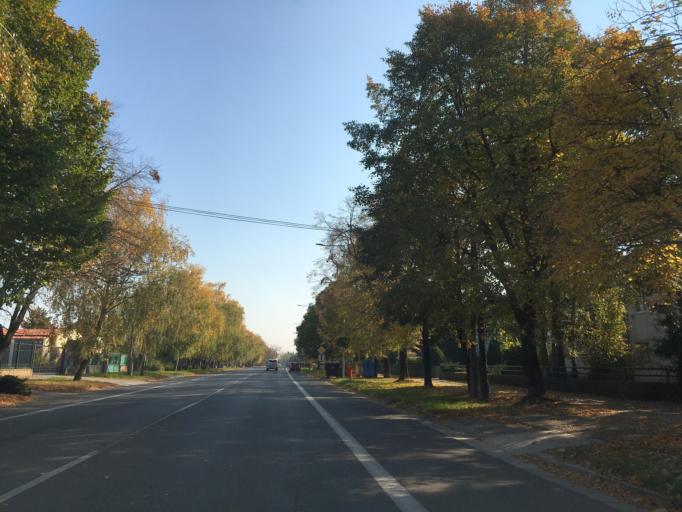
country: SK
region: Trnavsky
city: Samorin
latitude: 48.0318
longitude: 17.3063
